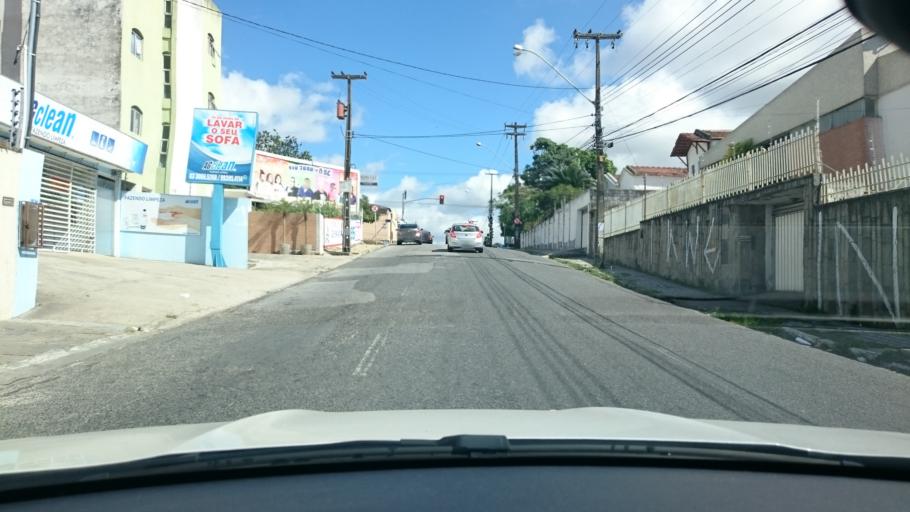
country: BR
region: Paraiba
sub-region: Campina Grande
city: Campina Grande
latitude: -7.2200
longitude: -35.8914
